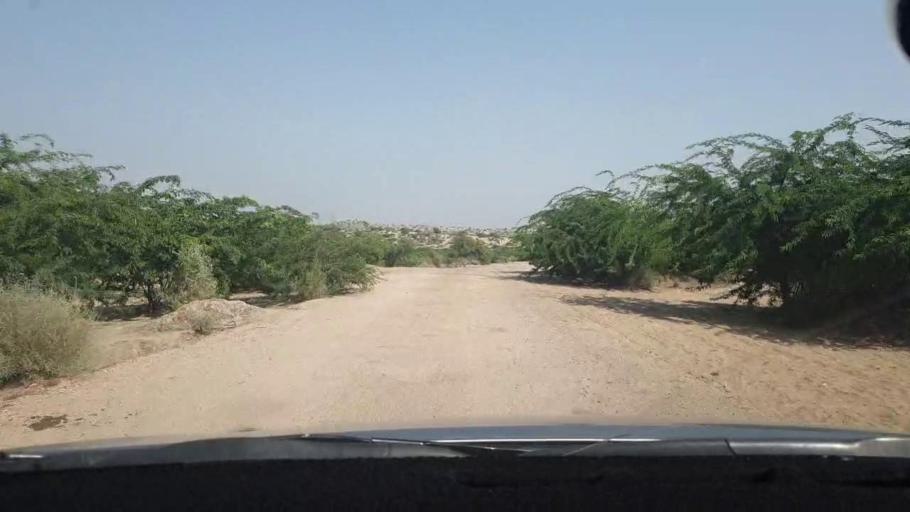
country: PK
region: Sindh
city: Pithoro
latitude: 25.7807
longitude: 69.4817
